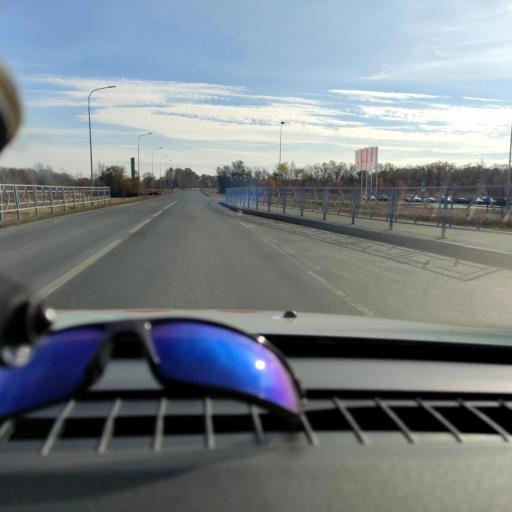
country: RU
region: Samara
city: Samara
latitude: 53.0871
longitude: 50.1385
